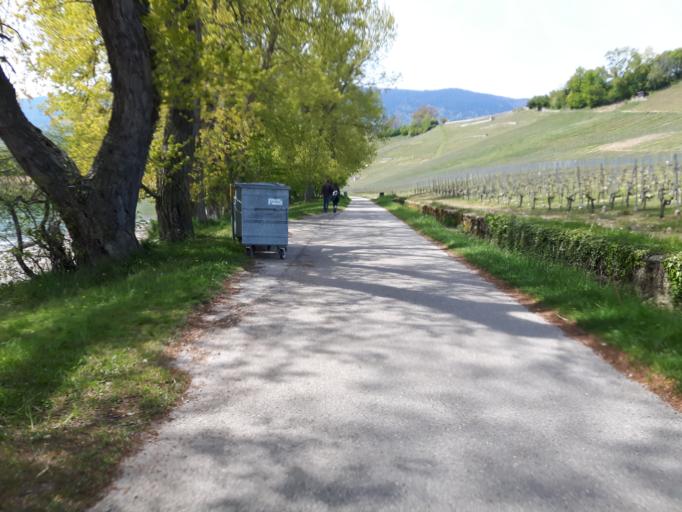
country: CH
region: Neuchatel
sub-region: Boudry District
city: Cortaillod
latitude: 46.9265
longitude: 6.8349
